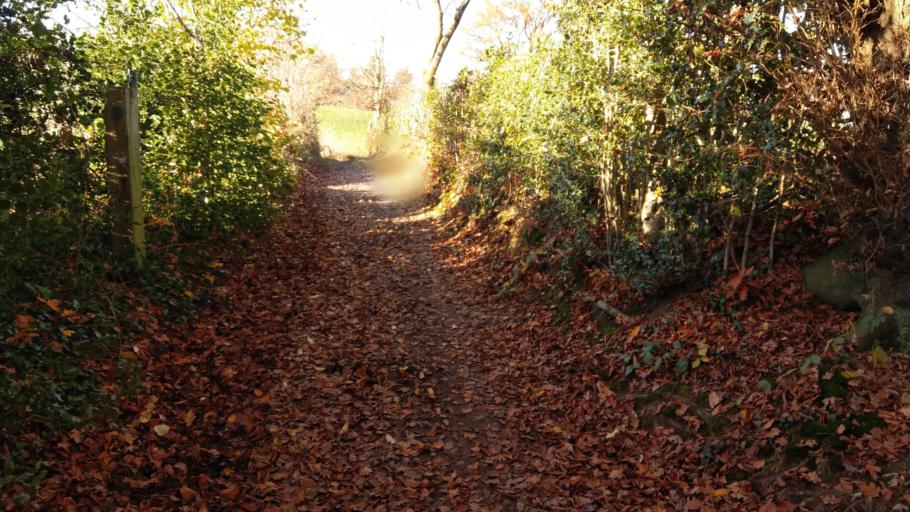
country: BE
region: Wallonia
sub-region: Province de Liege
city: La Calamine
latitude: 50.7357
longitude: 6.0024
